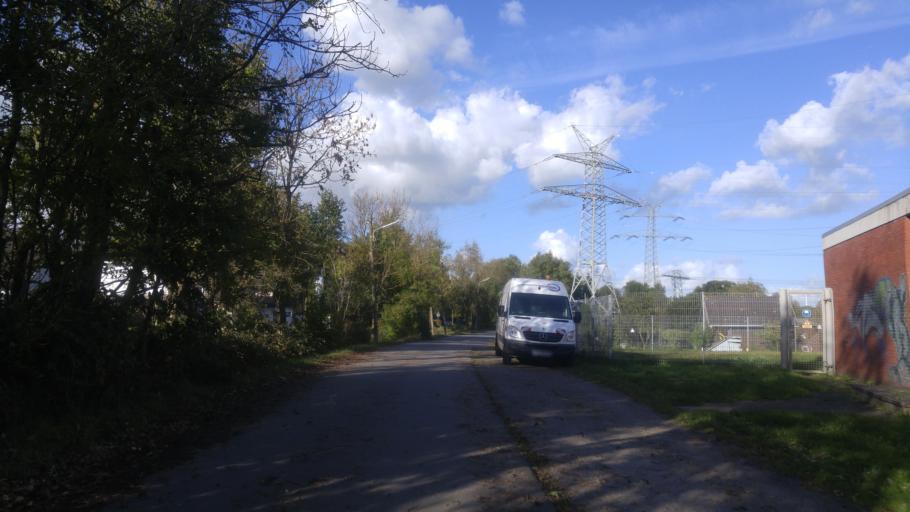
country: DE
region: Bremen
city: Bremen
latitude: 53.1079
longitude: 8.8181
